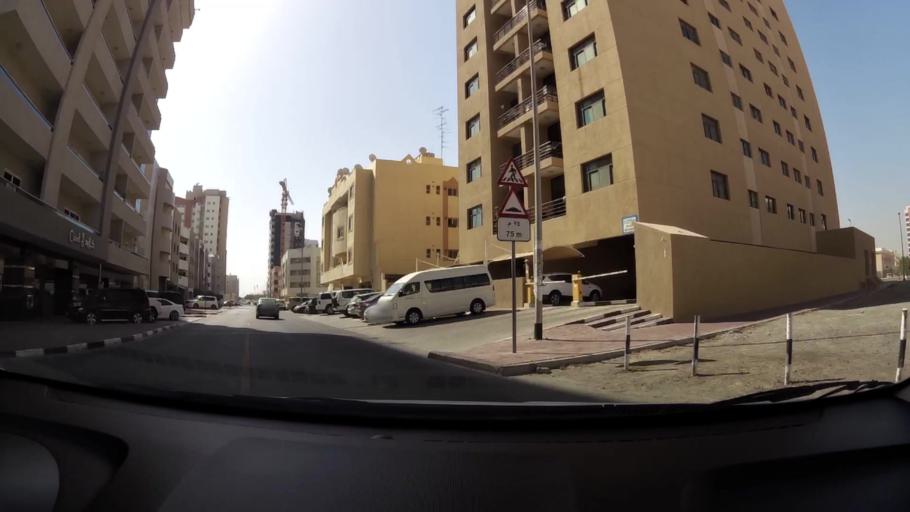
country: AE
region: Ash Shariqah
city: Sharjah
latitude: 25.2738
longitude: 55.3719
